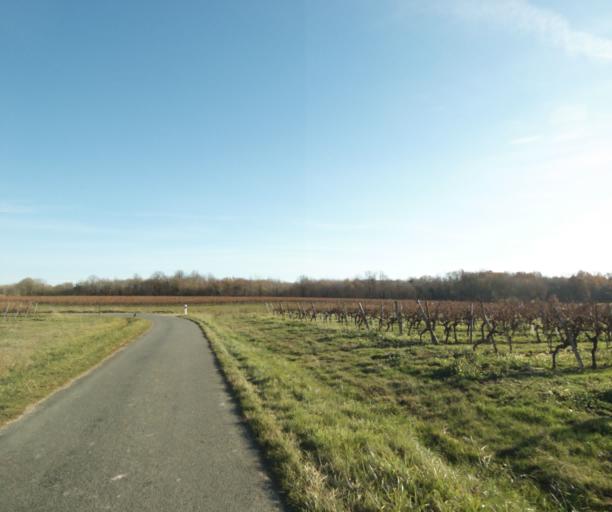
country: FR
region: Poitou-Charentes
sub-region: Departement de la Charente-Maritime
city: Burie
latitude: 45.7767
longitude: -0.4445
